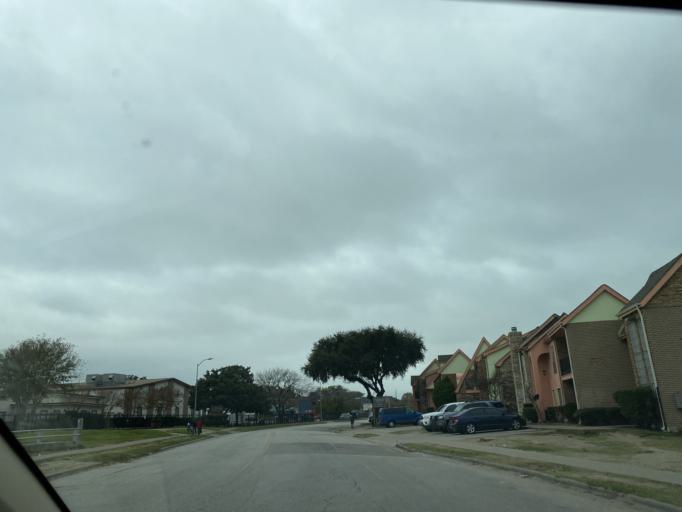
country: US
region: Texas
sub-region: Harris County
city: Piney Point Village
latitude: 29.7261
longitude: -95.4952
